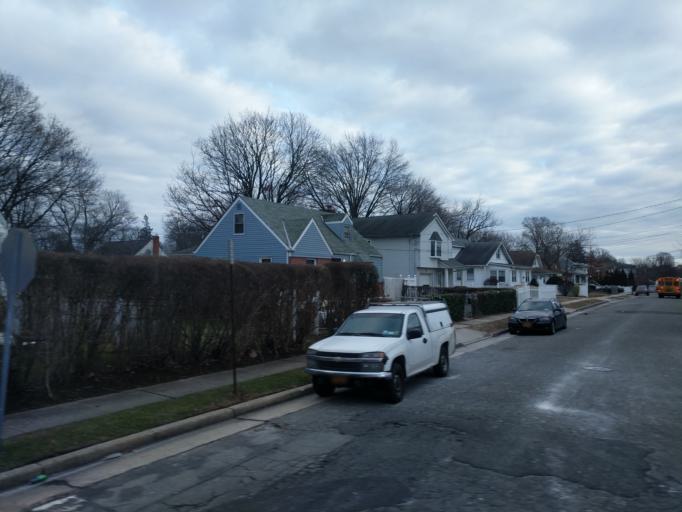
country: US
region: New York
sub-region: Nassau County
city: East Garden City
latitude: 40.7204
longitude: -73.6094
